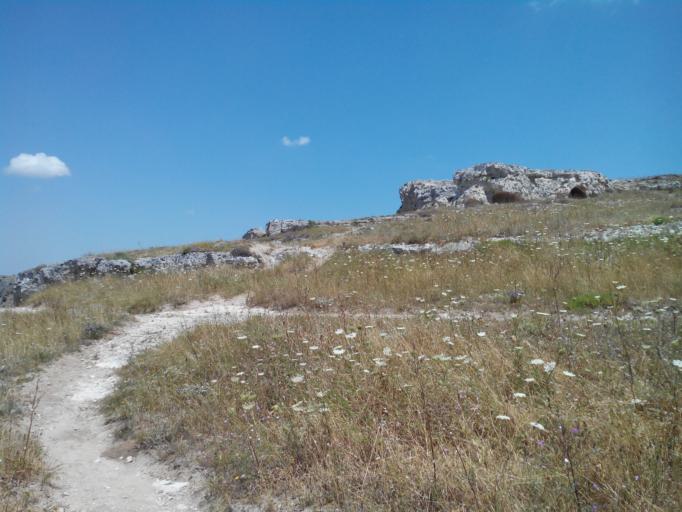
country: IT
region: Basilicate
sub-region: Provincia di Matera
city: Matera
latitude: 40.6638
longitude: 16.6156
